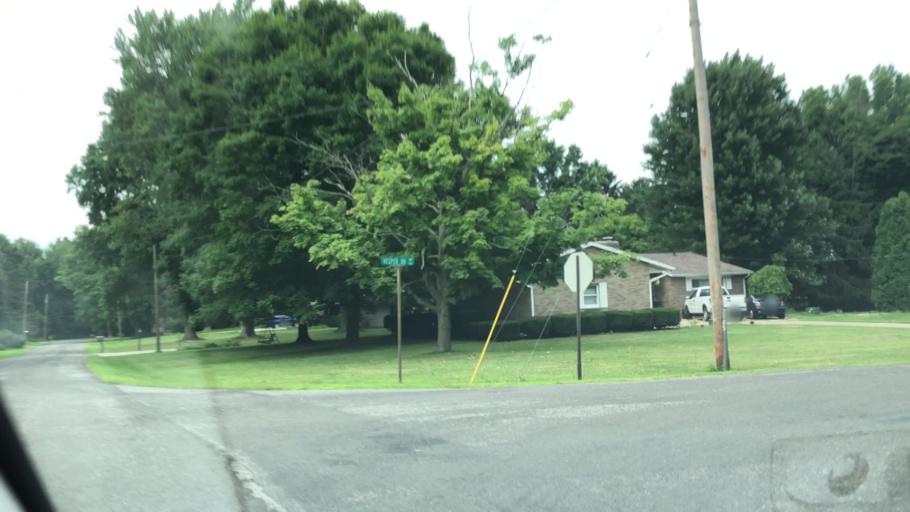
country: US
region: Ohio
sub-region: Summit County
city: Fairlawn
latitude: 41.1375
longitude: -81.6214
